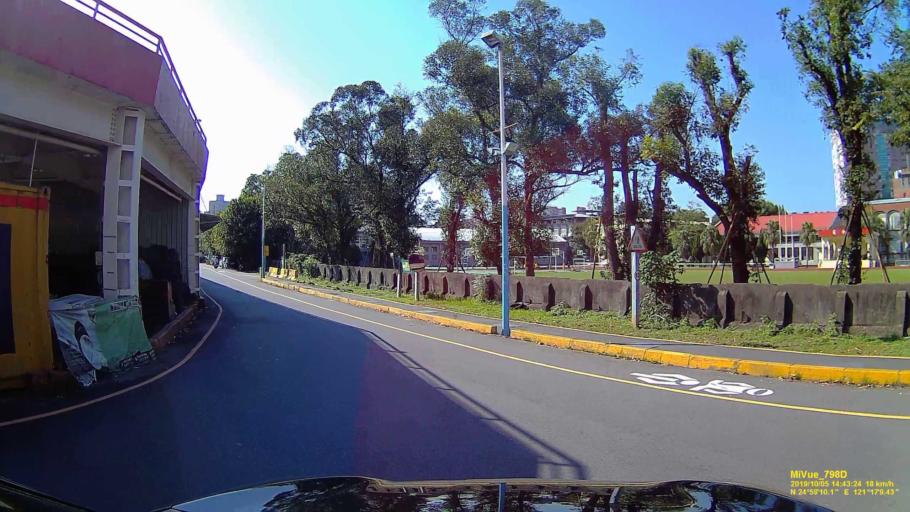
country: TW
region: Taiwan
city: Taoyuan City
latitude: 24.9862
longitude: 121.2858
